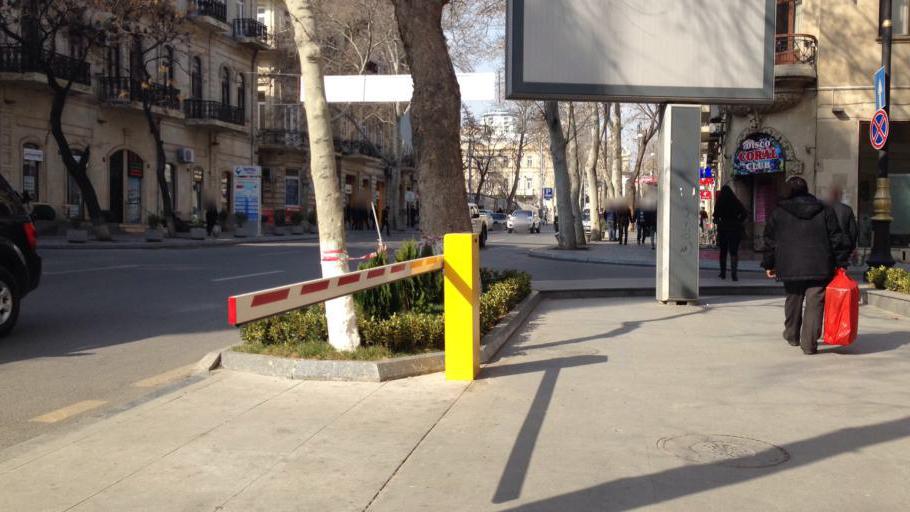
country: AZ
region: Baki
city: Baku
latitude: 40.3755
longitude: 49.8433
